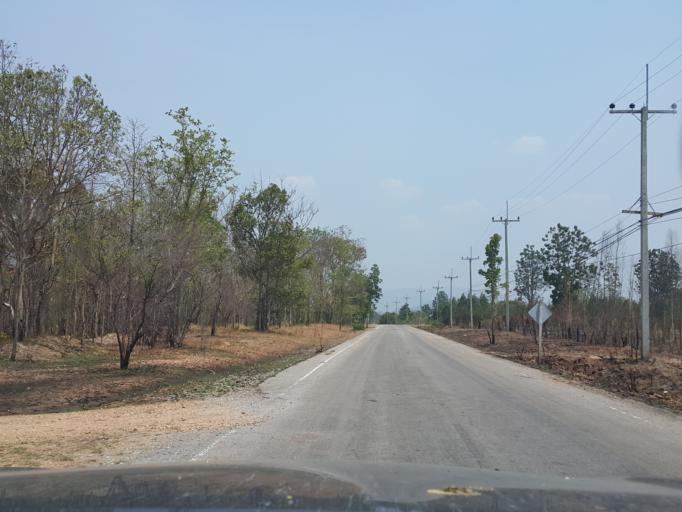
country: TH
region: Lampang
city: Mae Phrik
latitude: 17.5399
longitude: 99.1406
